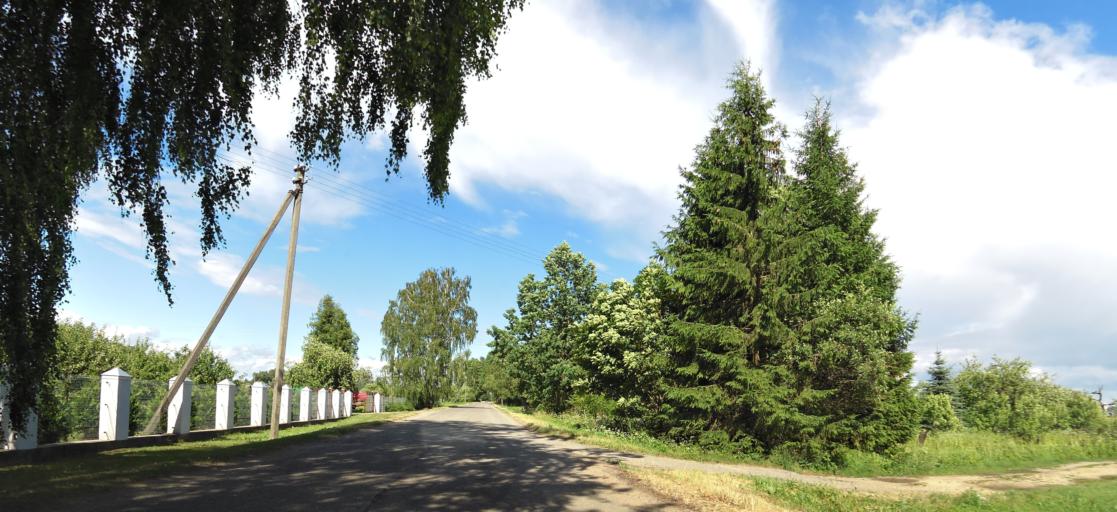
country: LT
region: Panevezys
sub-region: Birzai
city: Birzai
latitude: 56.3690
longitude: 24.6359
